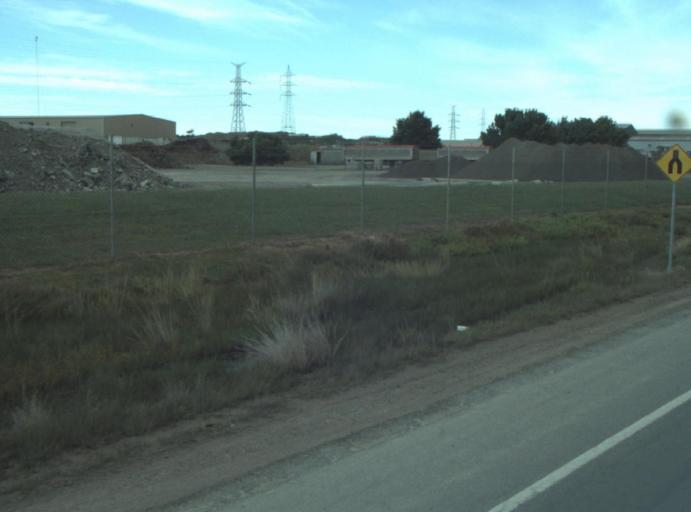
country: AU
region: Victoria
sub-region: Greater Geelong
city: Leopold
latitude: -38.1583
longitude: 144.4309
